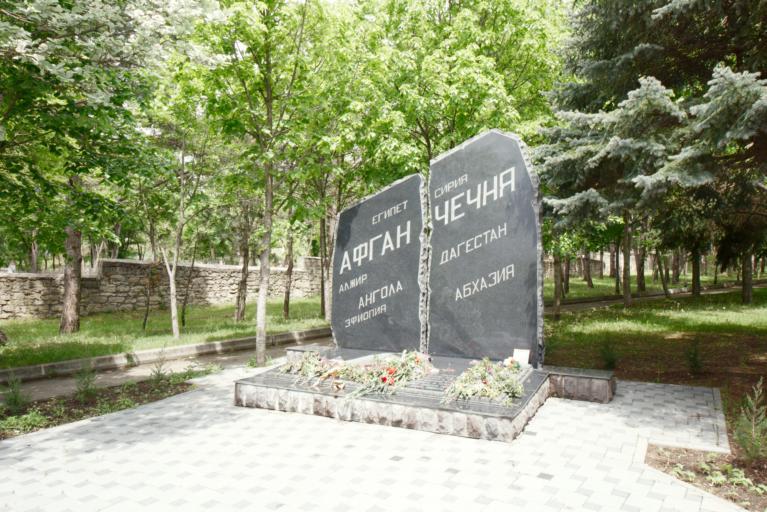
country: RU
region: Stavropol'skiy
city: Pyatigorsk
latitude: 44.0447
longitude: 43.0734
